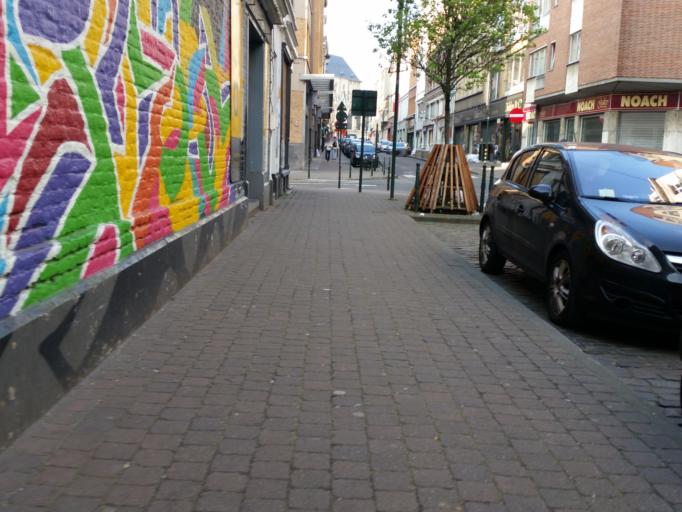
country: BE
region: Brussels Capital
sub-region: Bruxelles-Capitale
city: Brussels
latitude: 50.8391
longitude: 4.3489
